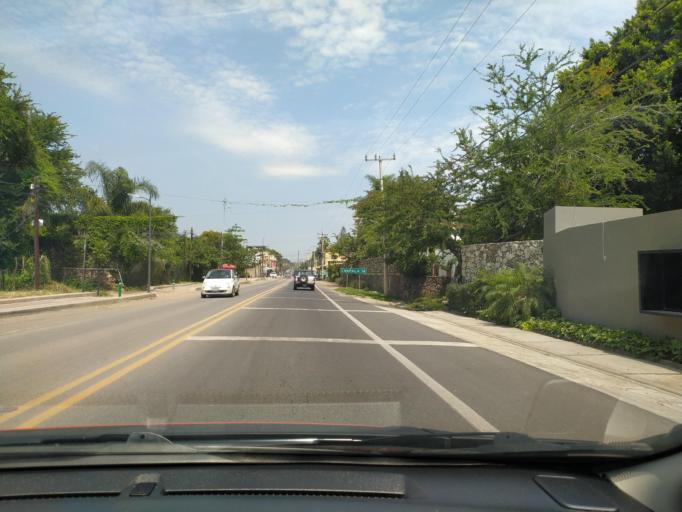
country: MX
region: Jalisco
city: San Juan Cosala
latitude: 20.2895
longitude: -103.3502
